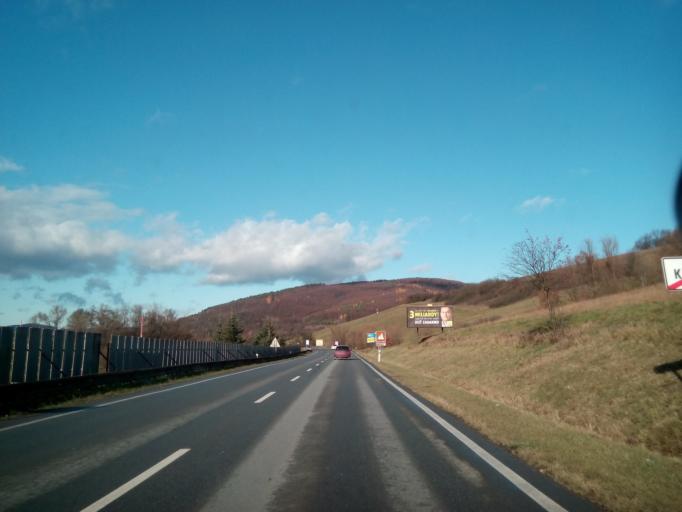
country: SK
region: Presovsky
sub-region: Okres Bardejov
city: Bardejov
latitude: 49.2501
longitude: 21.2553
